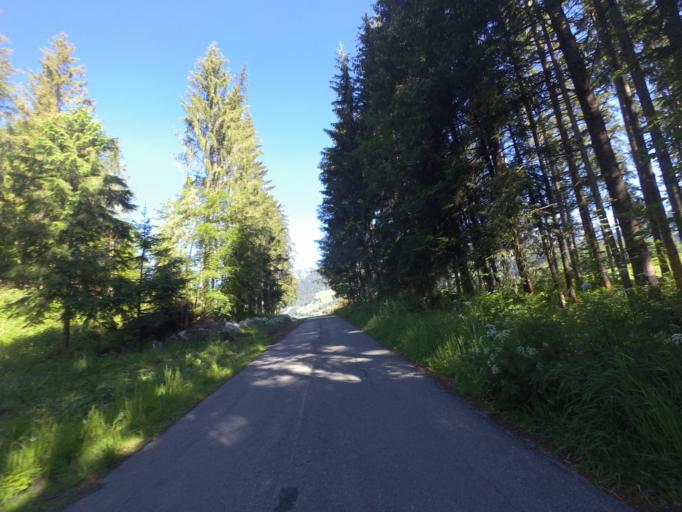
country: AT
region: Salzburg
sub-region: Politischer Bezirk Sankt Johann im Pongau
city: Goldegg
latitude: 47.3238
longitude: 13.1159
